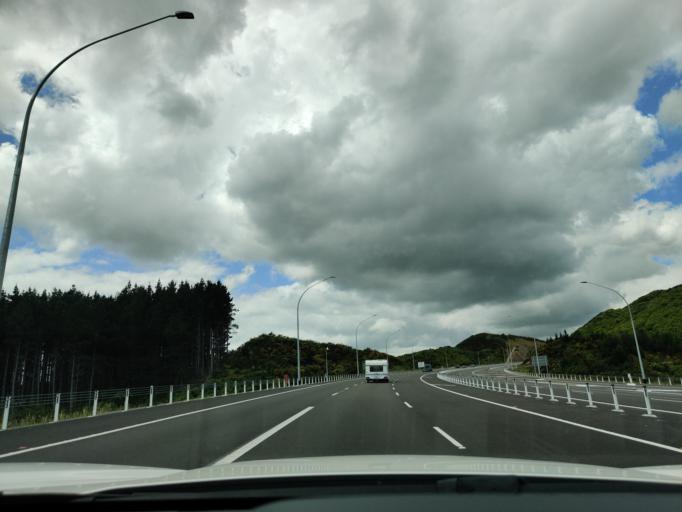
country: NZ
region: Wellington
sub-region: Porirua City
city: Porirua
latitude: -41.1500
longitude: 174.8477
